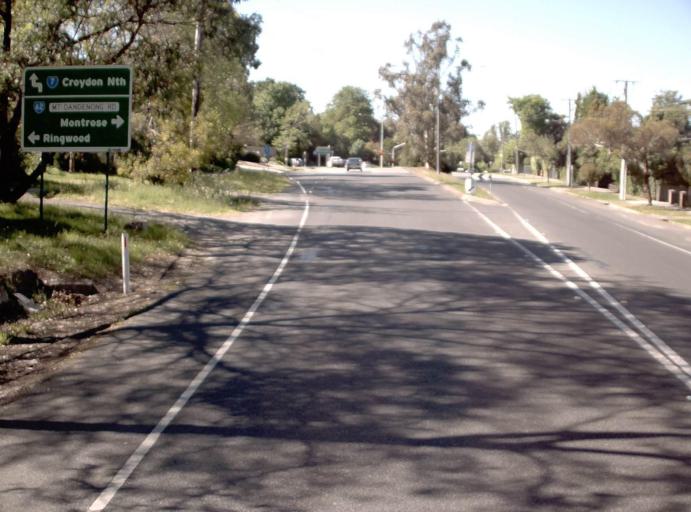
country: AU
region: Victoria
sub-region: Maroondah
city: Croydon South
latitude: -37.8027
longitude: 145.2734
